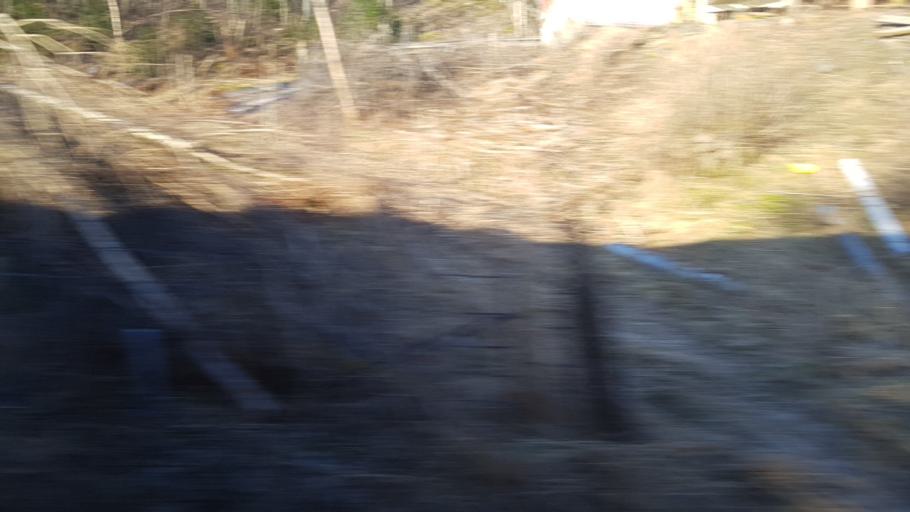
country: NO
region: Sor-Trondelag
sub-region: Malvik
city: Hommelvik
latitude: 63.4137
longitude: 10.7895
